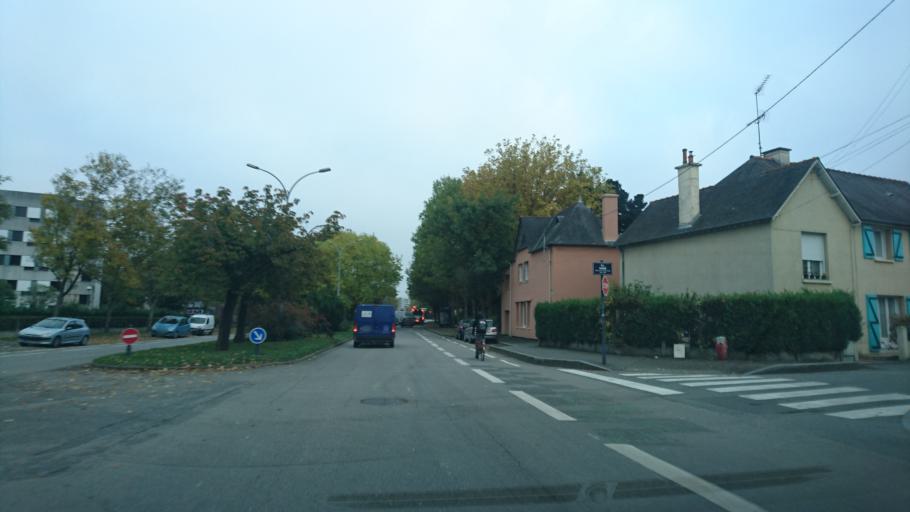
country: FR
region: Brittany
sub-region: Departement d'Ille-et-Vilaine
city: Rennes
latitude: 48.1153
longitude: -1.7029
